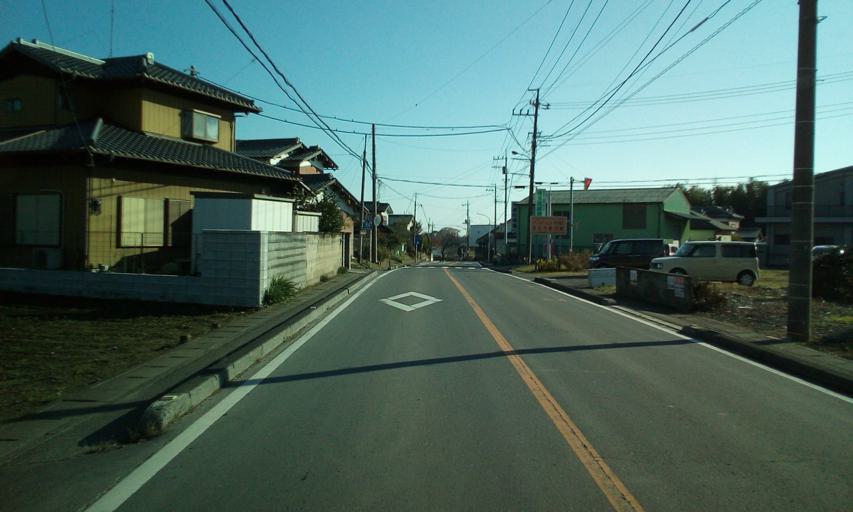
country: JP
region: Chiba
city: Noda
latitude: 35.9473
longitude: 139.8374
